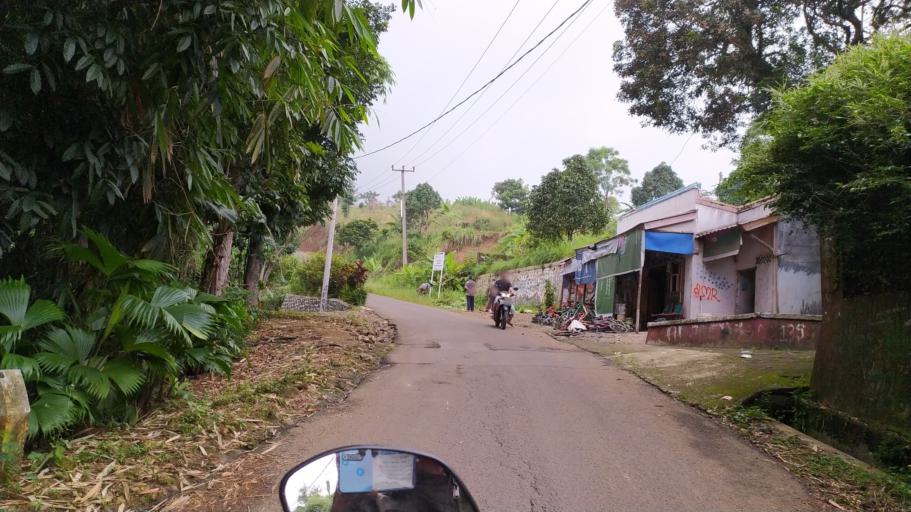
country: ID
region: West Java
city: Ciampea
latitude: -6.6436
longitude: 106.7045
